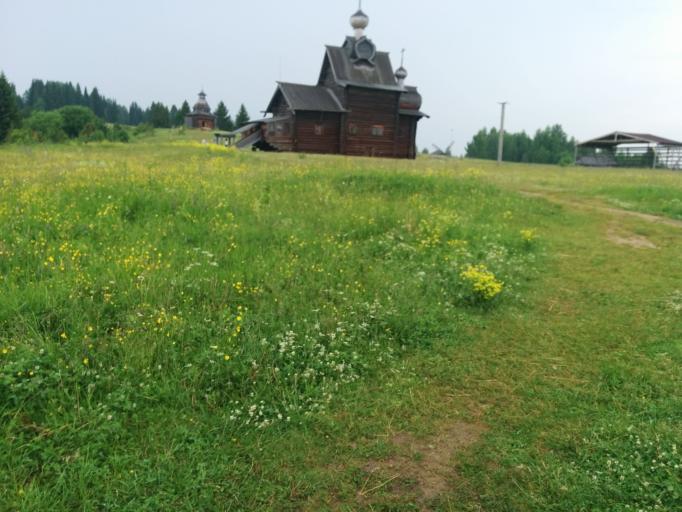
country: RU
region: Perm
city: Polazna
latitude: 58.2597
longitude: 56.2599
